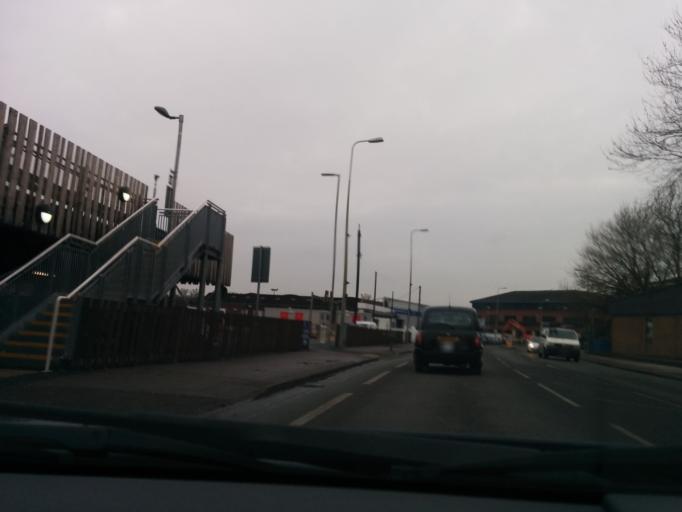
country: GB
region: England
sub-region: Oxfordshire
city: Oxford
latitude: 51.7492
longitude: -1.2651
